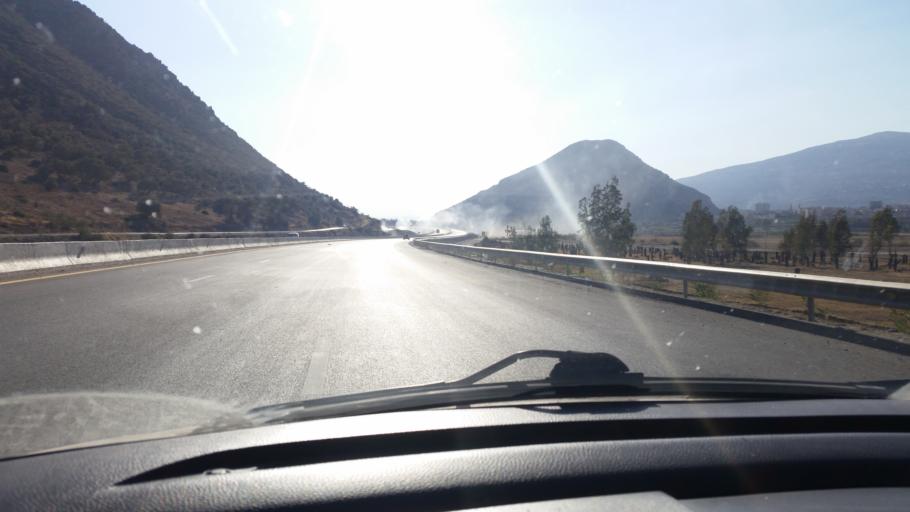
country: DZ
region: Bejaia
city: Akbou
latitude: 36.4515
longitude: 4.5610
